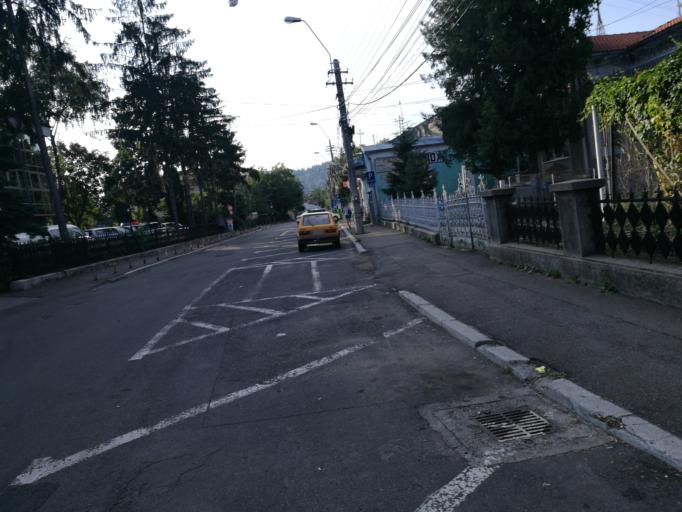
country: RO
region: Neamt
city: Piatra Neamt
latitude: 46.9334
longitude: 26.3648
